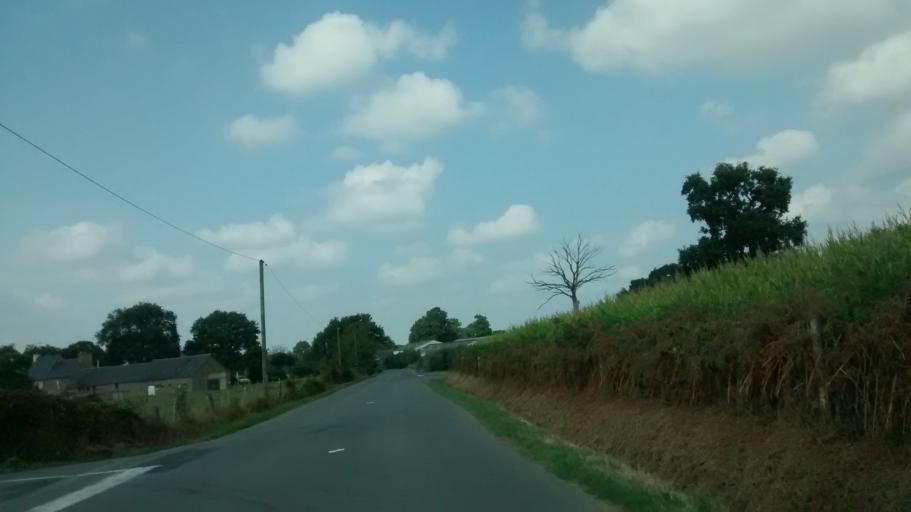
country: FR
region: Brittany
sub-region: Departement d'Ille-et-Vilaine
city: Livre-sur-Changeon
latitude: 48.2304
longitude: -1.2838
